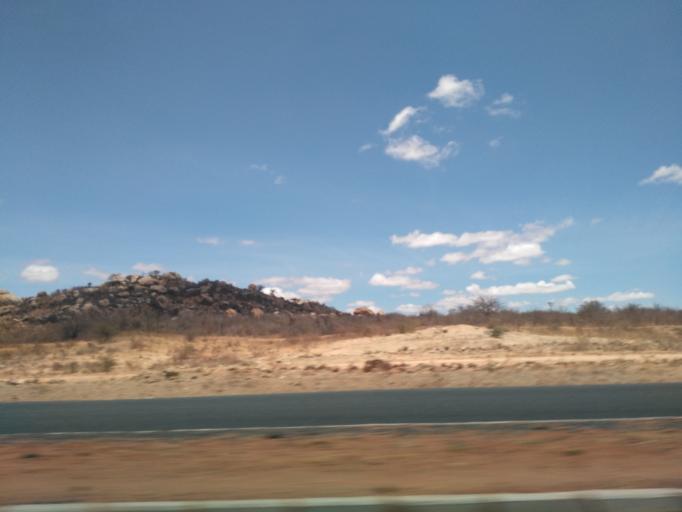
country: TZ
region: Dodoma
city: Kisasa
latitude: -6.1802
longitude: 35.8377
